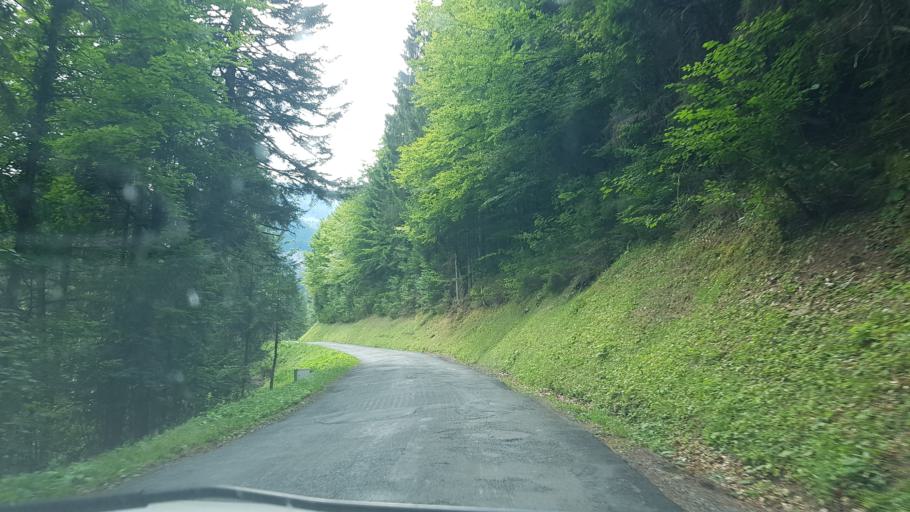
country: FR
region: Rhone-Alpes
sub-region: Departement de la Haute-Savoie
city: Samoens
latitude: 46.0332
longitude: 6.7689
